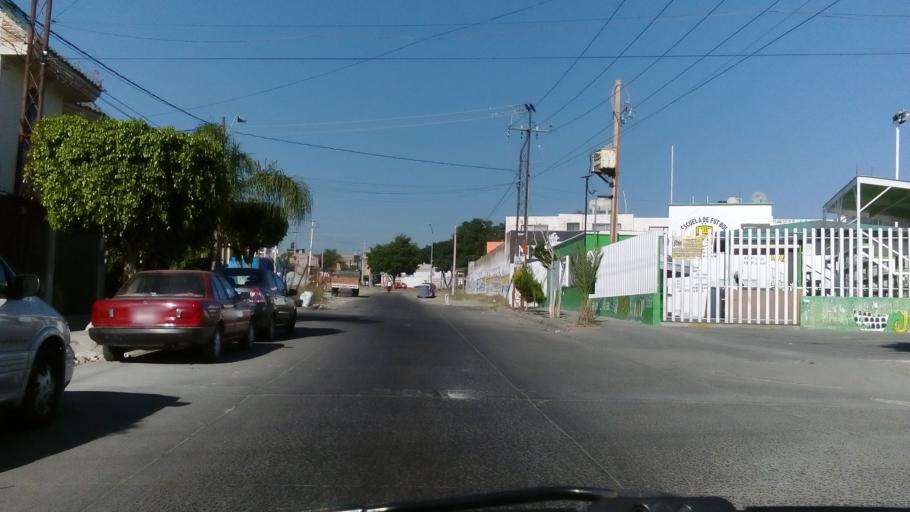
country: MX
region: Guanajuato
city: Leon
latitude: 21.1160
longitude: -101.7075
